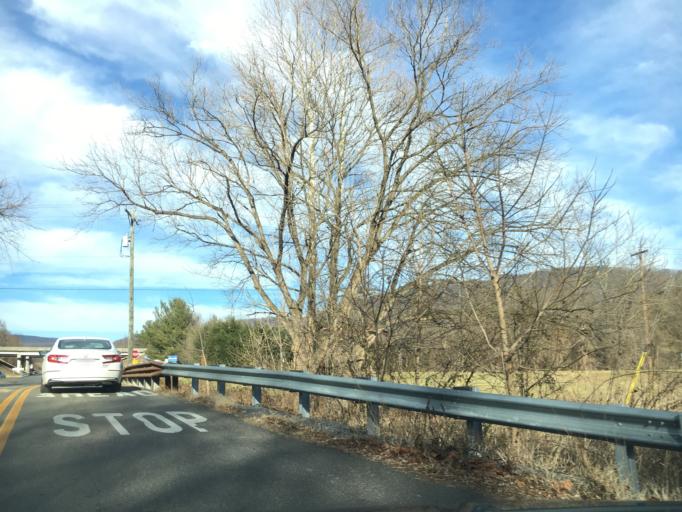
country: US
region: Virginia
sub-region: Warren County
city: Apple Mountain Lake
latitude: 38.9053
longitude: -77.9975
